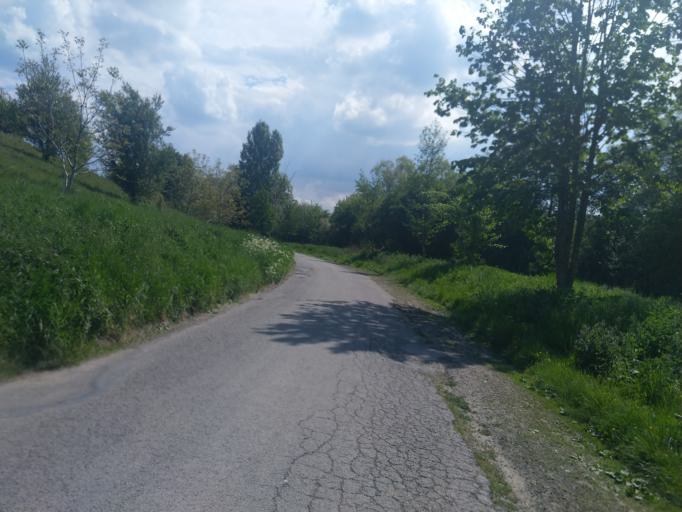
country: BE
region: Wallonia
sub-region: Province du Hainaut
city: Chasse Royale
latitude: 50.4172
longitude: 3.9691
